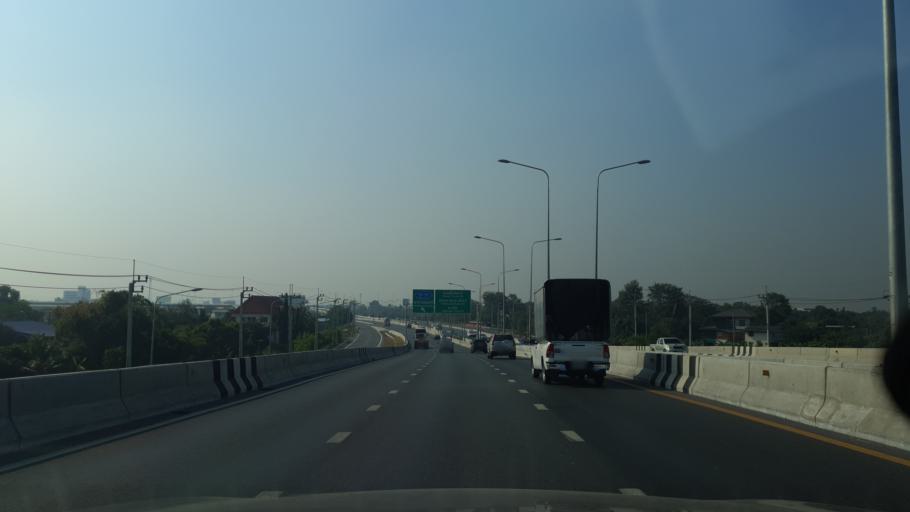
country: TH
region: Nonthaburi
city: Bang Bua Thong
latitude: 13.9607
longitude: 100.4593
